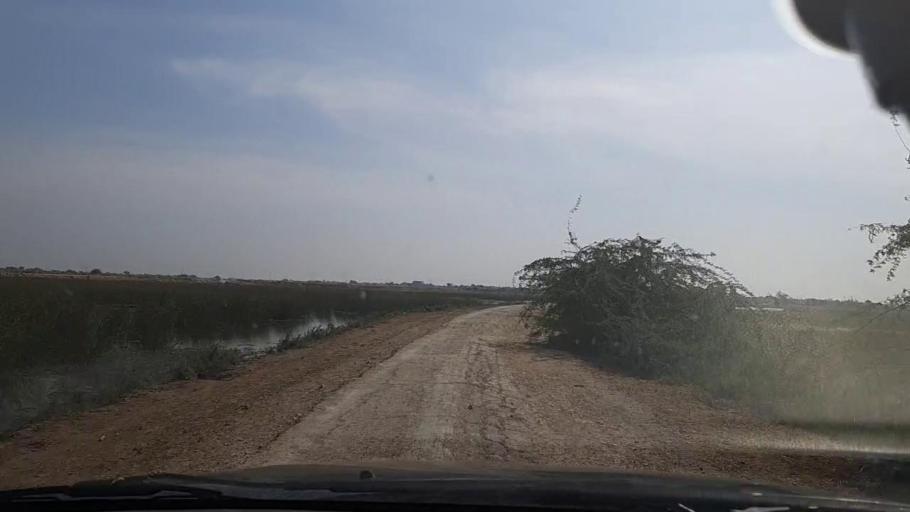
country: PK
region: Sindh
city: Mirpur Batoro
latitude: 24.7489
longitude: 68.2694
